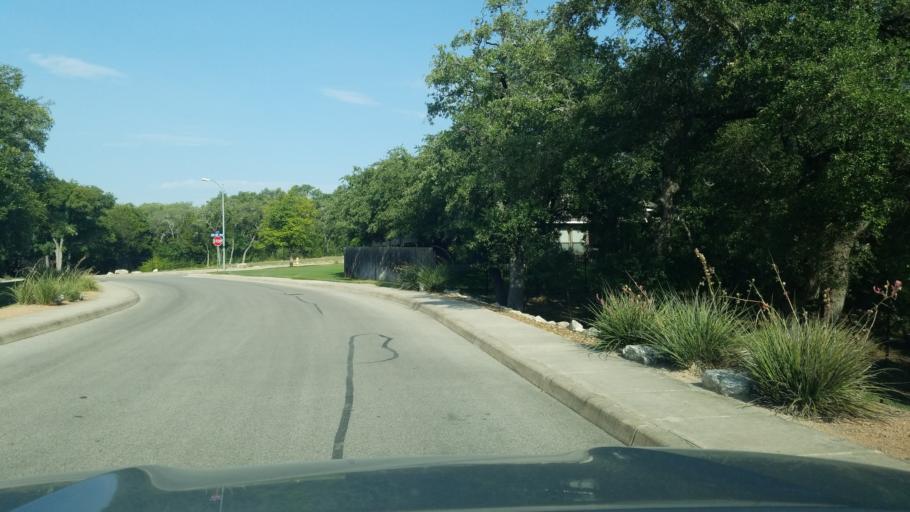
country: US
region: Texas
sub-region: Medina County
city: La Coste
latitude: 29.4410
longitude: -98.7530
